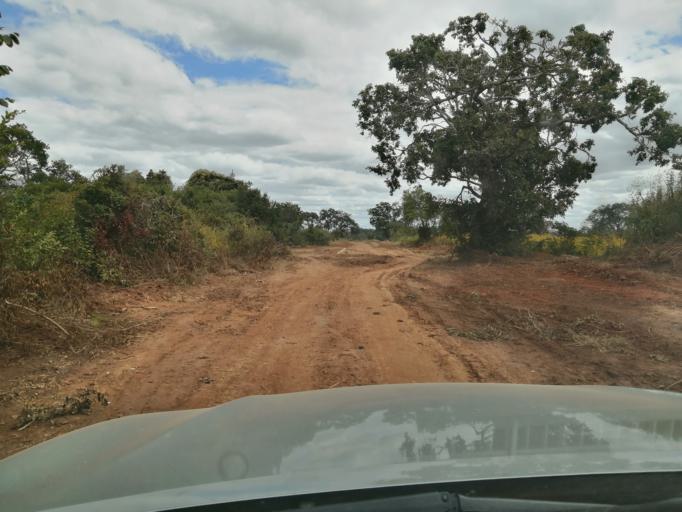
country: ZM
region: Central
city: Mumbwa
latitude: -14.5851
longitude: 27.2041
